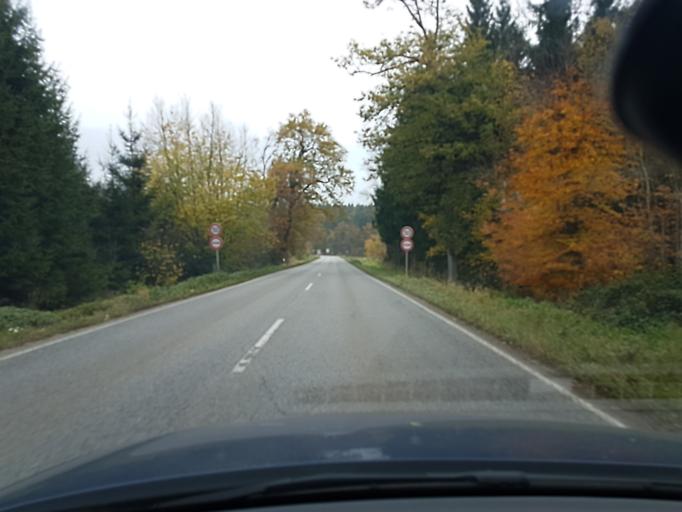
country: DE
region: Bavaria
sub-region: Upper Palatinate
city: Hagelstadt
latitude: 48.8802
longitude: 12.2112
